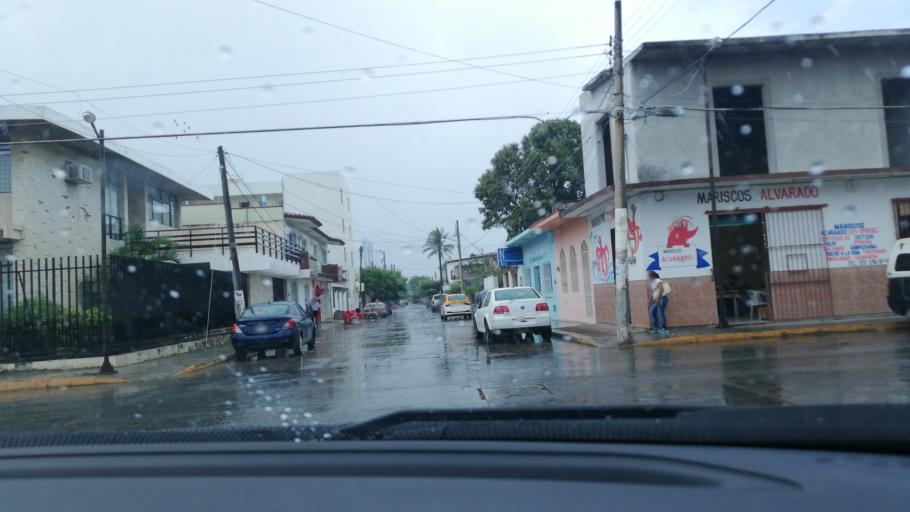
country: MX
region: Oaxaca
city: San Jeronimo Ixtepec
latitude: 16.5565
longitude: -95.0966
